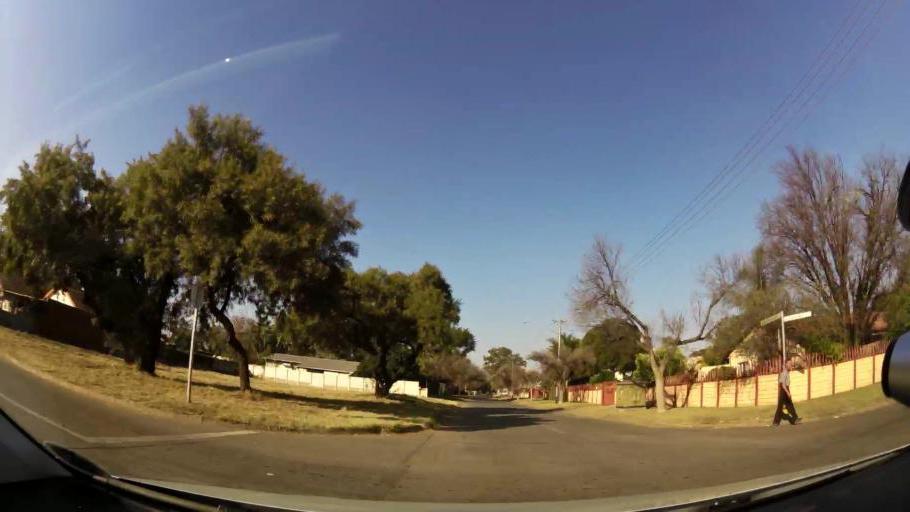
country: ZA
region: Gauteng
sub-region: City of Tshwane Metropolitan Municipality
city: Pretoria
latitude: -25.7131
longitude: 28.1392
